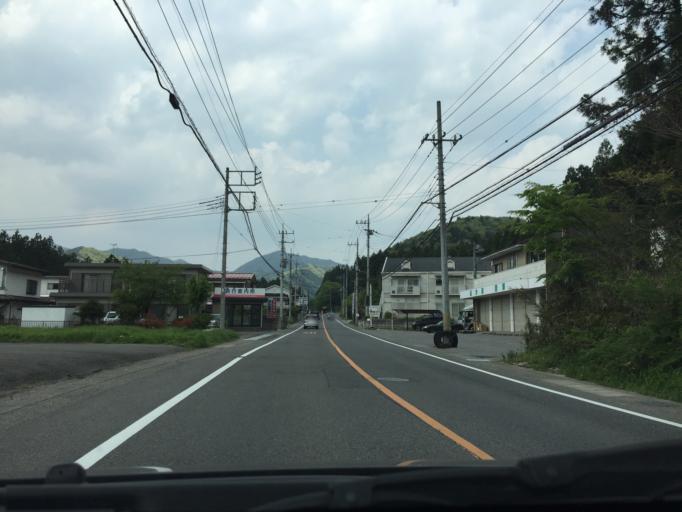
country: JP
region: Tochigi
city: Imaichi
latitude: 36.7900
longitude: 139.7056
